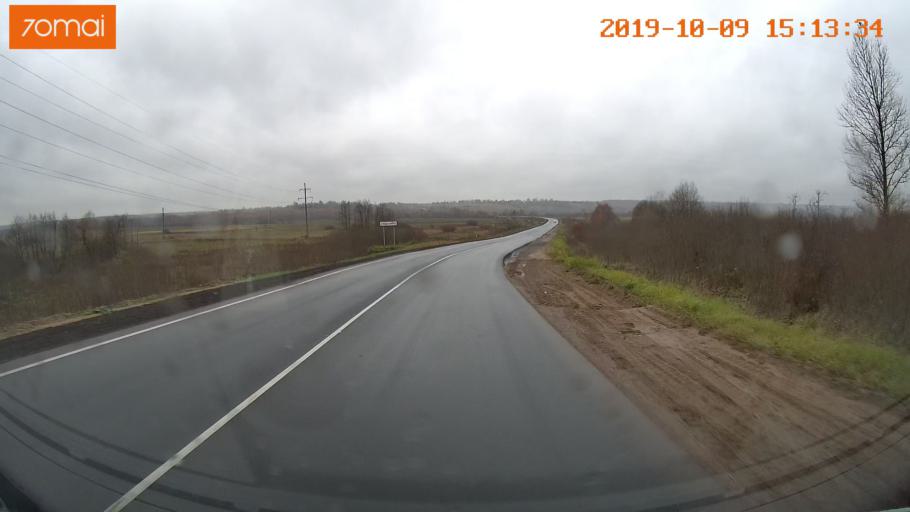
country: RU
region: Kostroma
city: Susanino
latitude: 58.1445
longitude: 41.6141
